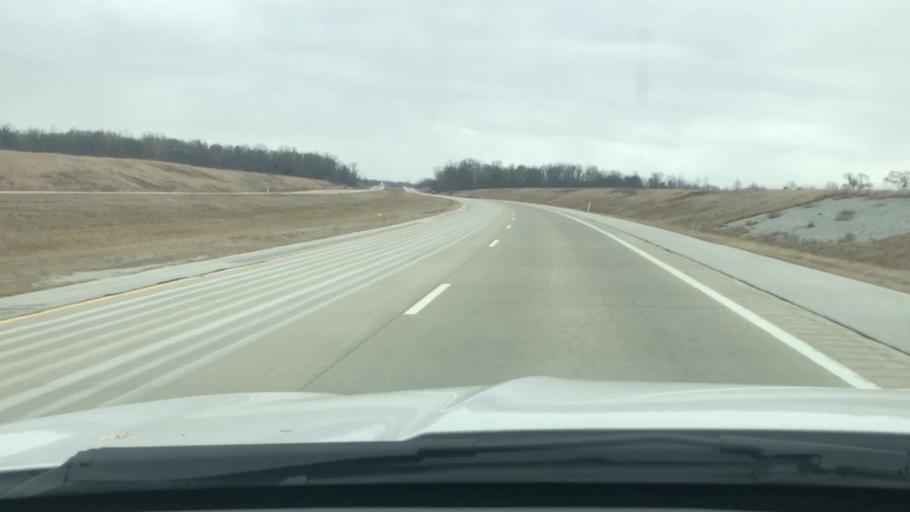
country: US
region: Indiana
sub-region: Carroll County
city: Delphi
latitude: 40.5277
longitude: -86.7110
